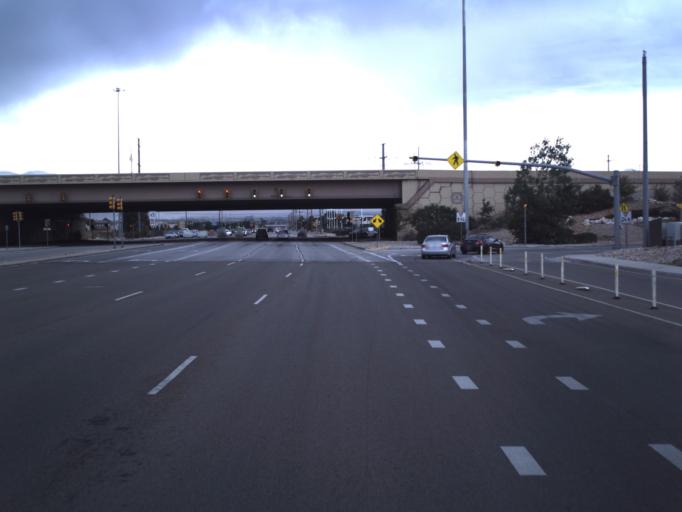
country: US
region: Utah
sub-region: Salt Lake County
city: Draper
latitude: 40.5269
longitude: -111.8894
